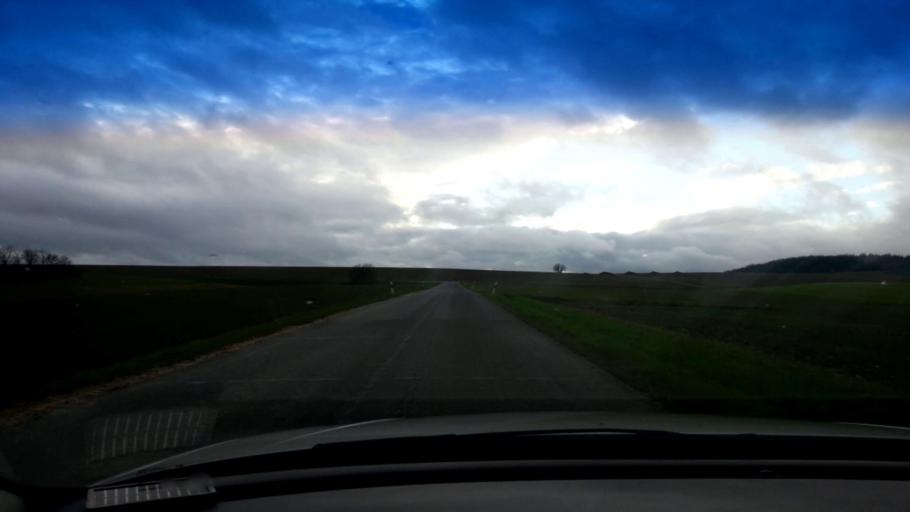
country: DE
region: Bavaria
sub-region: Upper Franconia
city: Ebensfeld
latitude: 50.0298
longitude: 10.9718
